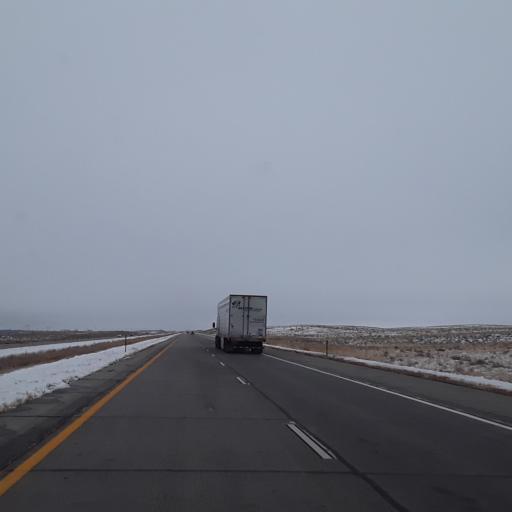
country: US
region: Colorado
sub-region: Logan County
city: Sterling
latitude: 40.5727
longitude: -103.2031
